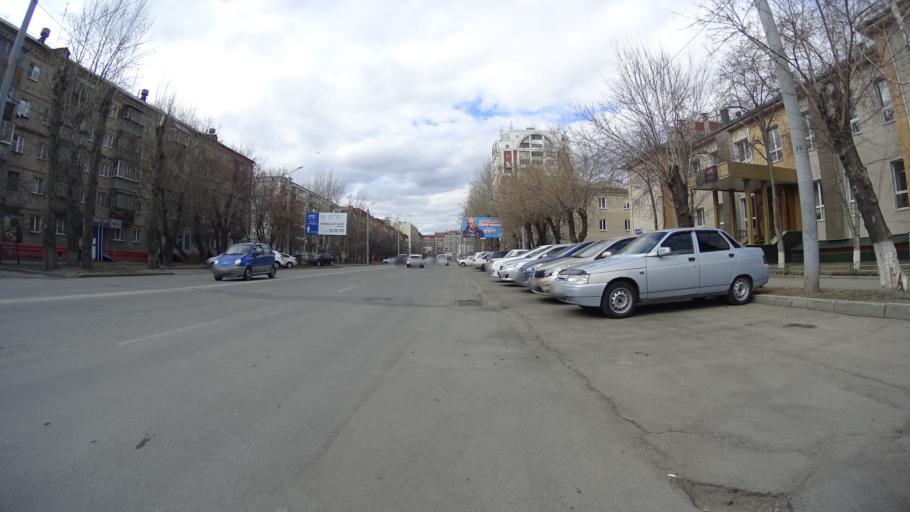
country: RU
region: Chelyabinsk
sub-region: Gorod Chelyabinsk
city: Chelyabinsk
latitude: 55.1494
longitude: 61.3806
